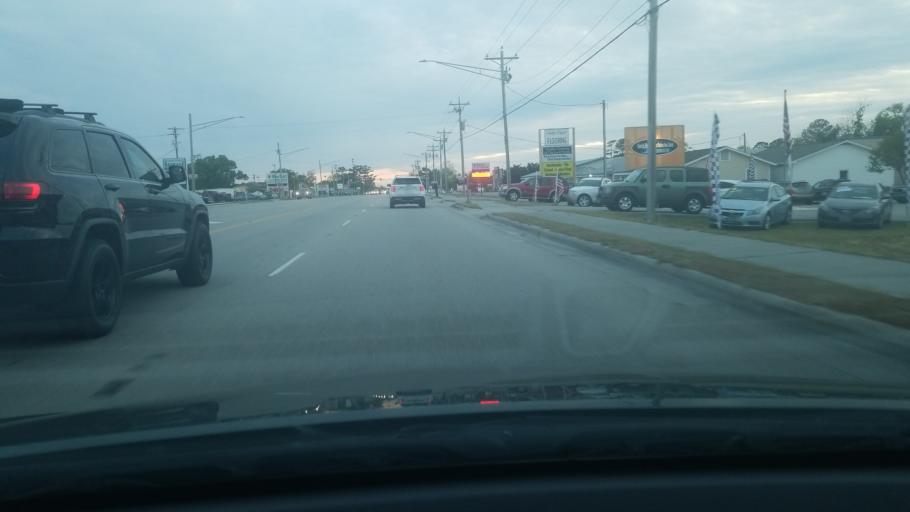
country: US
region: North Carolina
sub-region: Carteret County
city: Cedar Point
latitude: 34.6839
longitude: -77.0821
